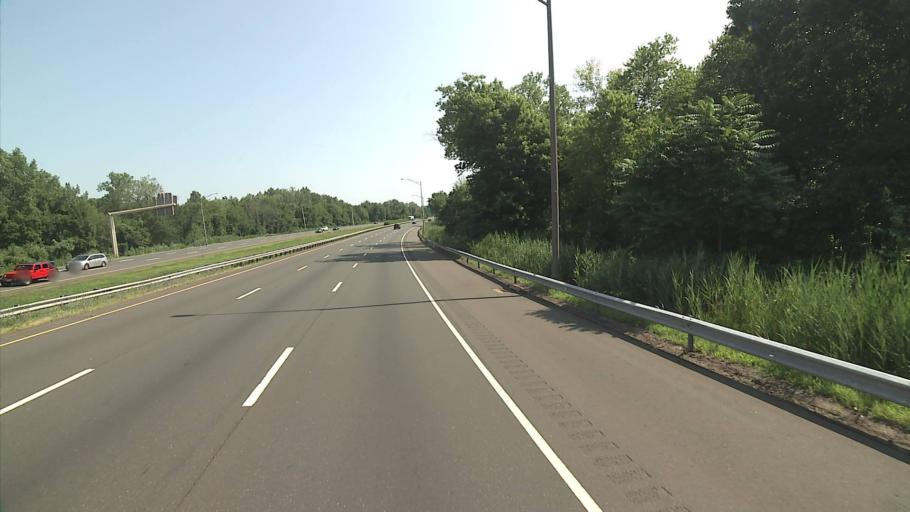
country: US
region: Connecticut
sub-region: New Haven County
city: North Haven
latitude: 41.3937
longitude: -72.8633
